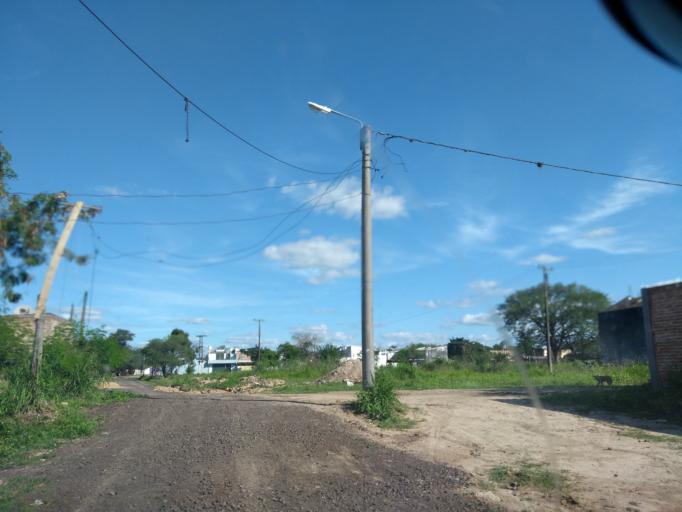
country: AR
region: Chaco
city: Barranqueras
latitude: -27.4724
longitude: -58.9596
